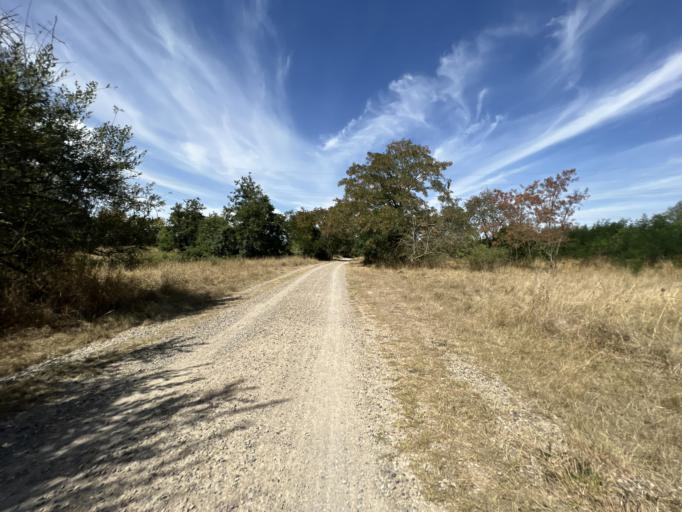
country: DE
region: North Rhine-Westphalia
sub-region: Regierungsbezirk Koln
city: Niederzier
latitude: 50.8340
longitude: 6.4458
